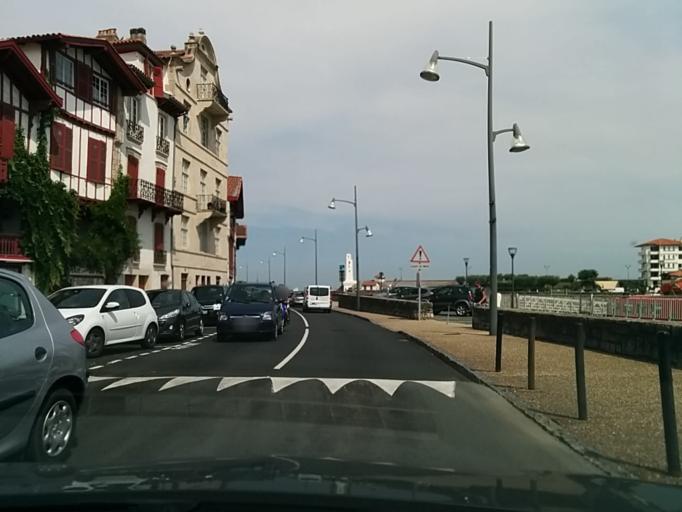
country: FR
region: Aquitaine
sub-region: Departement des Pyrenees-Atlantiques
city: Saint-Jean-de-Luz
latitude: 43.3853
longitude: -1.6673
